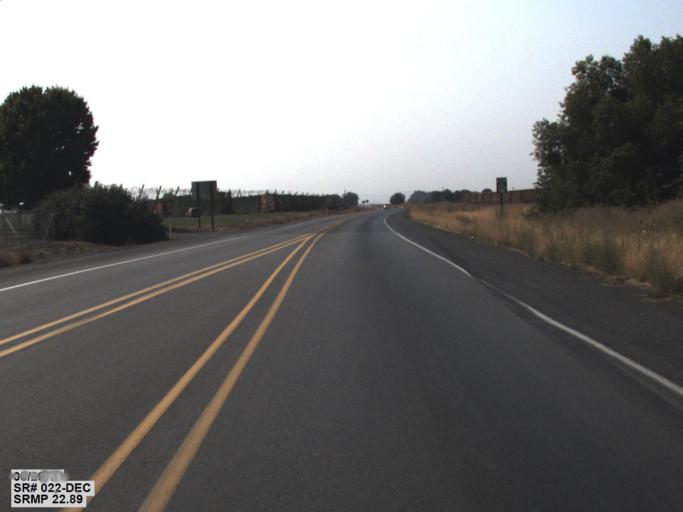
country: US
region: Washington
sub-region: Yakima County
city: Mabton
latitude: 46.2125
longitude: -120.0041
